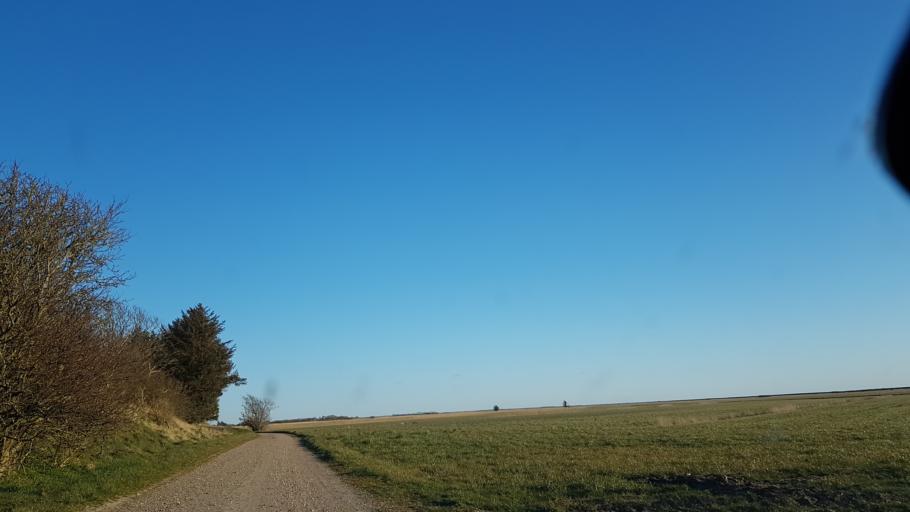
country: DK
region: South Denmark
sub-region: Esbjerg Kommune
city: Bramming
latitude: 55.4185
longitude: 8.6436
